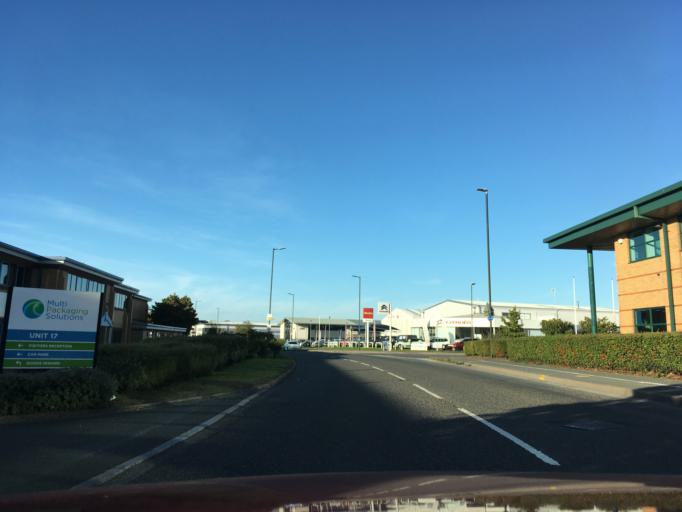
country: GB
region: England
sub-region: Worcestershire
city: Bredon
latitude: 51.9988
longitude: -2.1270
